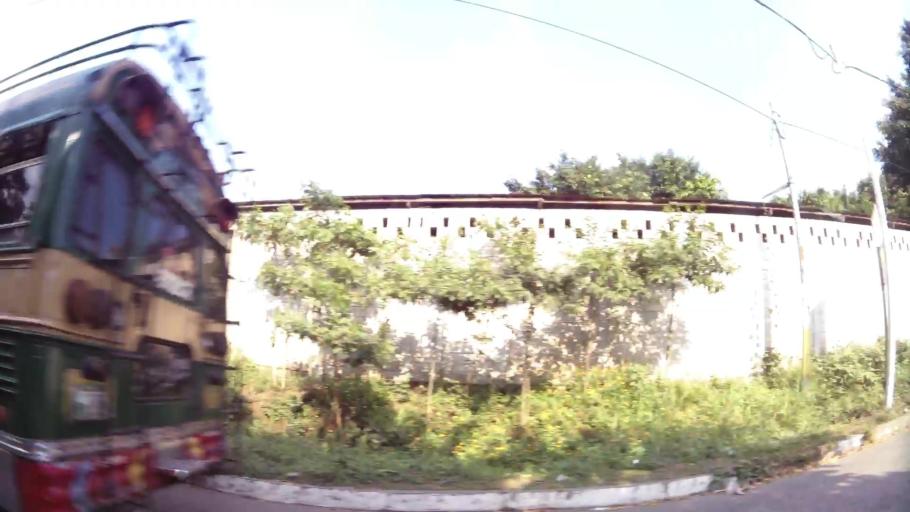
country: GT
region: Retalhuleu
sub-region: Municipio de Retalhuleu
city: Retalhuleu
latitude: 14.5306
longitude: -91.6896
